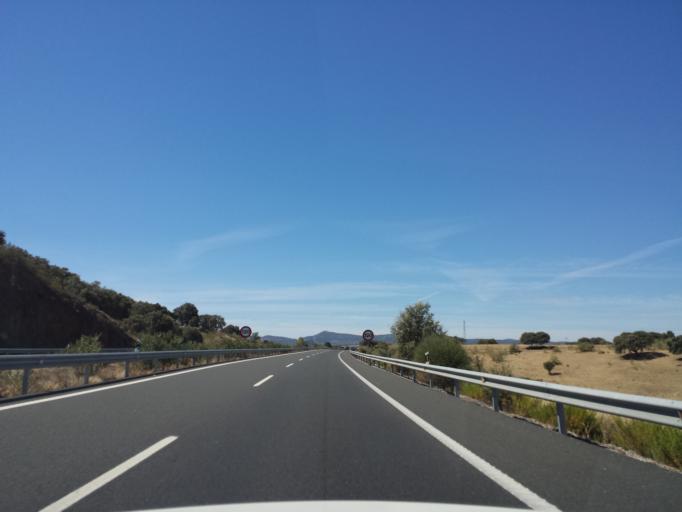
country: ES
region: Extremadura
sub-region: Provincia de Caceres
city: Almaraz
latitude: 39.8024
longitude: -5.6738
